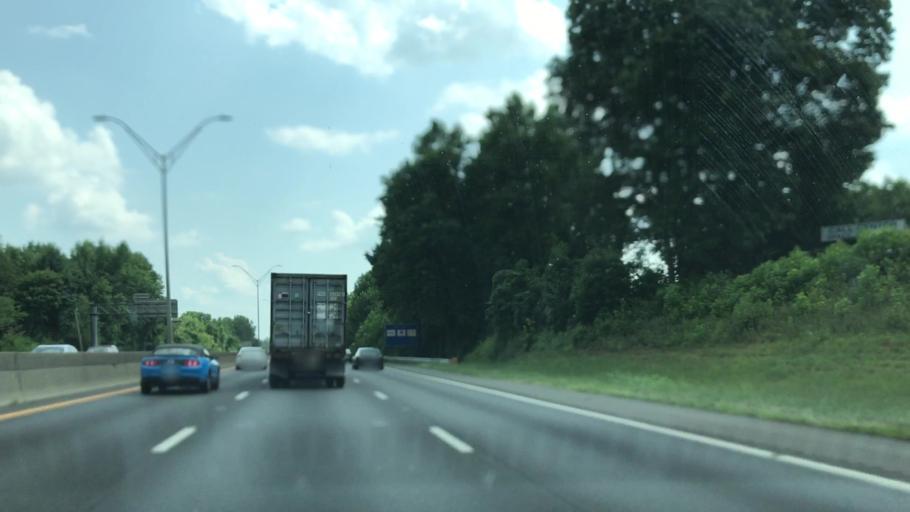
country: US
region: North Carolina
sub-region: Mecklenburg County
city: Pineville
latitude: 35.1538
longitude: -80.8932
